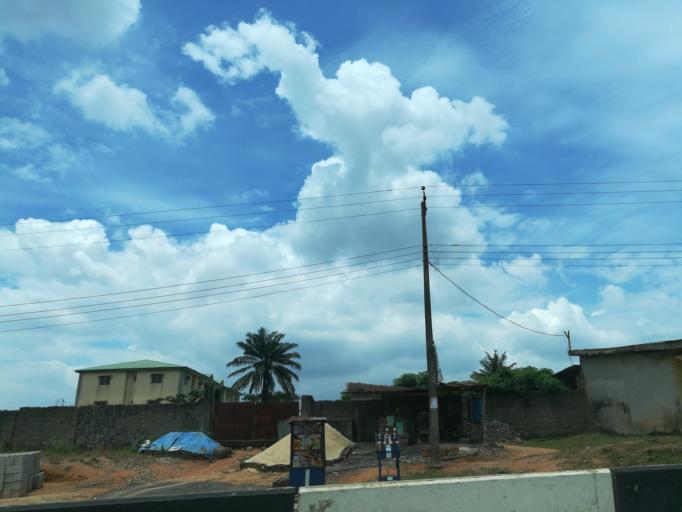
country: NG
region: Lagos
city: Ebute Ikorodu
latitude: 6.5999
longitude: 3.4991
